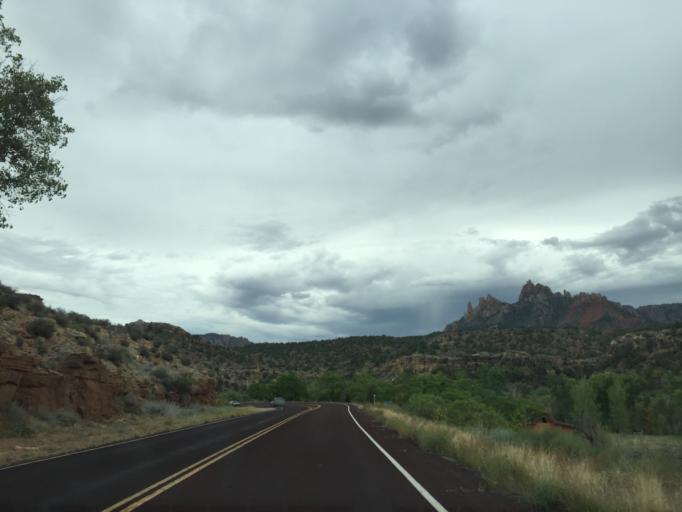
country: US
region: Utah
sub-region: Washington County
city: Hildale
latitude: 37.1621
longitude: -113.0224
